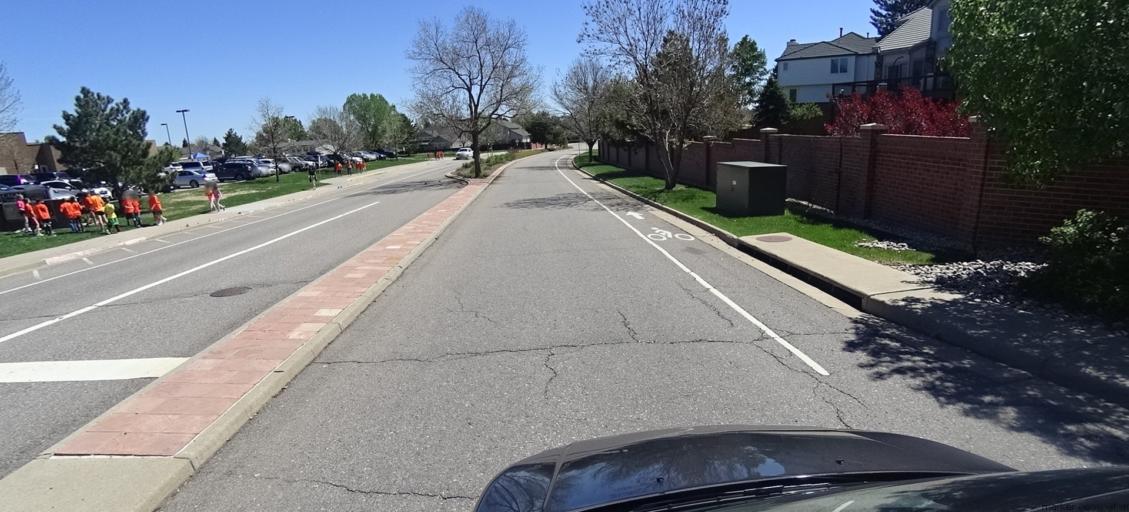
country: US
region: Colorado
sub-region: Douglas County
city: Acres Green
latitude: 39.5460
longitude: -104.9010
